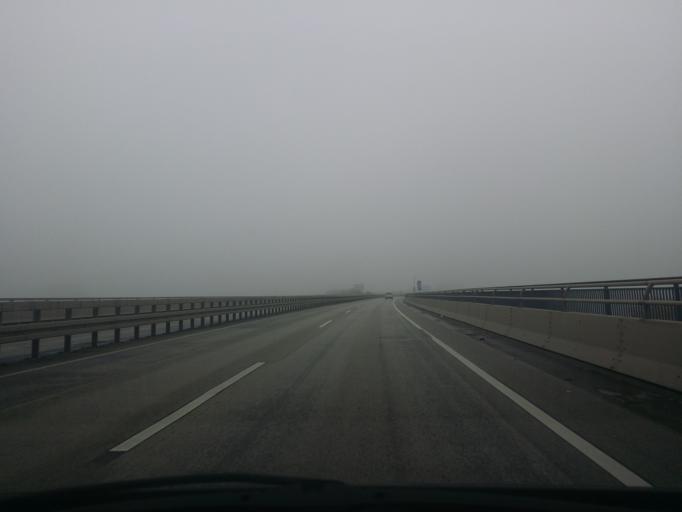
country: DE
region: Hesse
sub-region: Regierungsbezirk Darmstadt
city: Hochheim am Main
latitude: 50.0005
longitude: 8.3452
